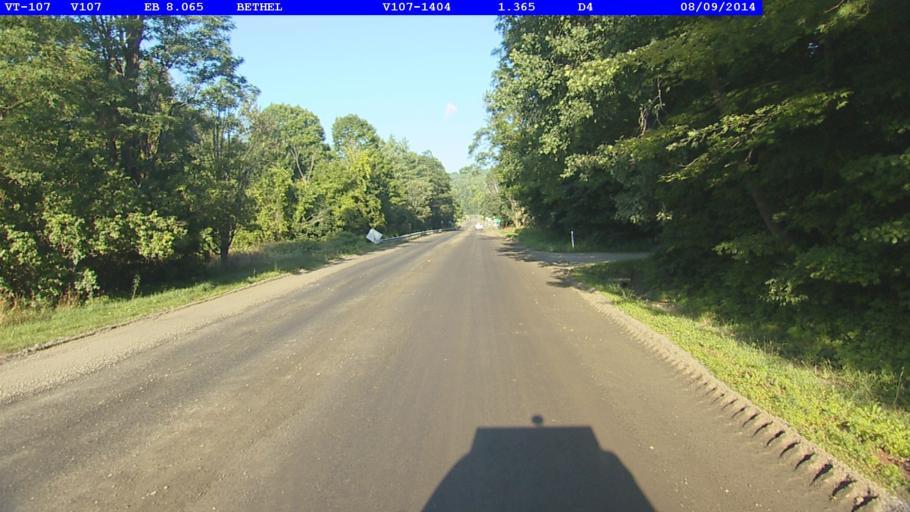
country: US
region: Vermont
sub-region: Orange County
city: Randolph
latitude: 43.8097
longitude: -72.6543
